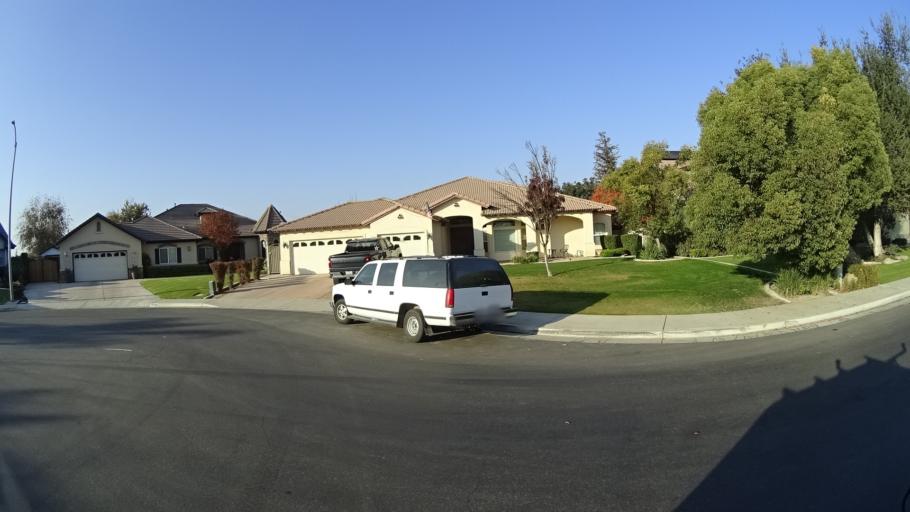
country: US
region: California
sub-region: Kern County
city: Rosedale
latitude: 35.3816
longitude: -119.1521
